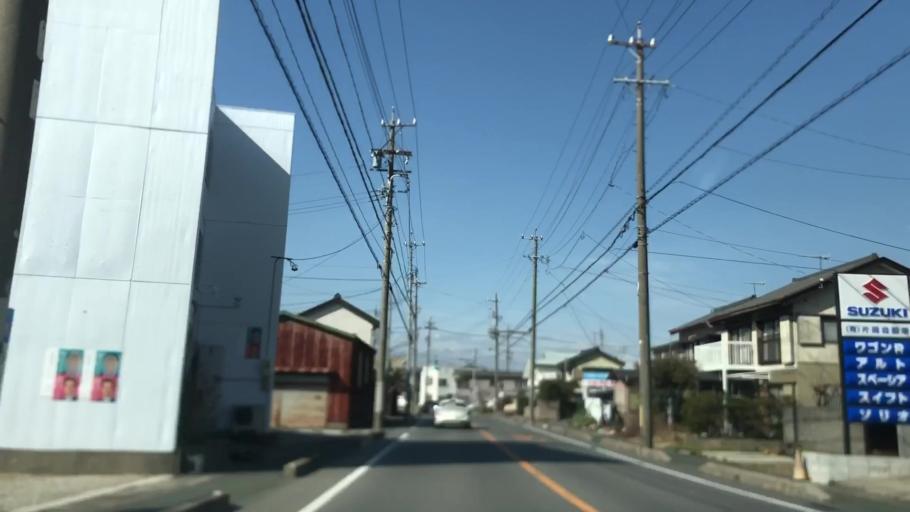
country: JP
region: Aichi
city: Gamagori
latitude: 34.8156
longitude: 137.2445
